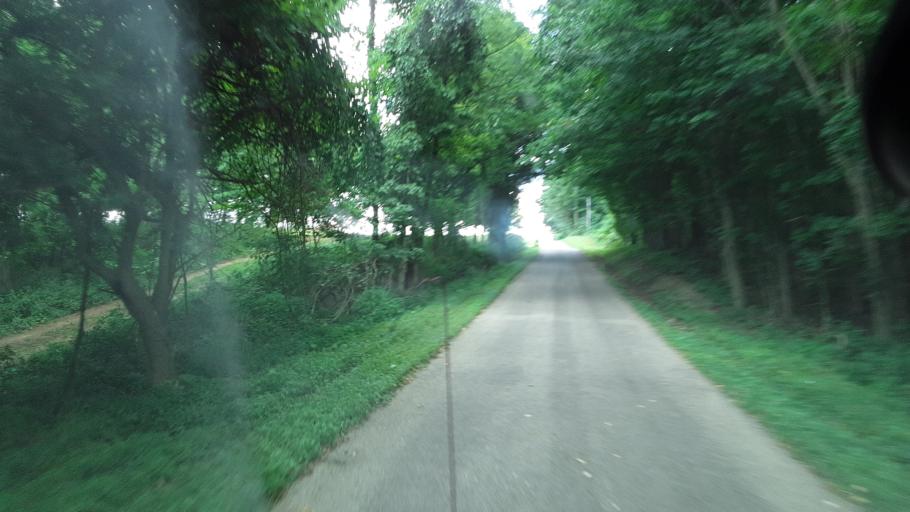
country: US
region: Ohio
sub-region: Licking County
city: Utica
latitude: 40.2619
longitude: -82.4120
